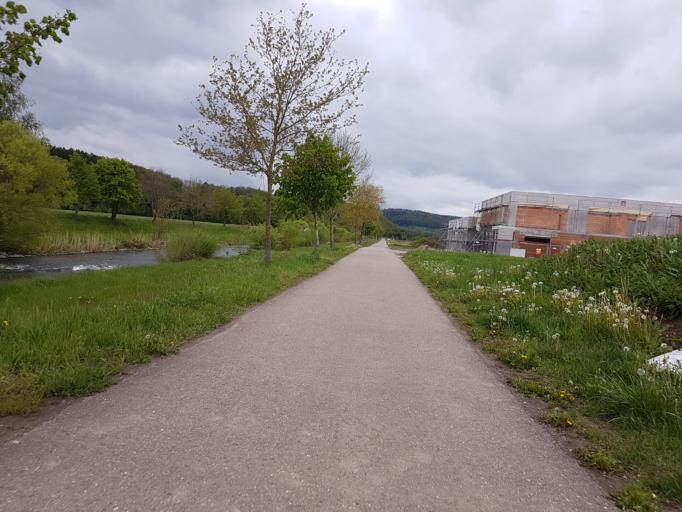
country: DE
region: Baden-Wuerttemberg
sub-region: Freiburg Region
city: Wutoschingen
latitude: 47.6392
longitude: 8.3473
